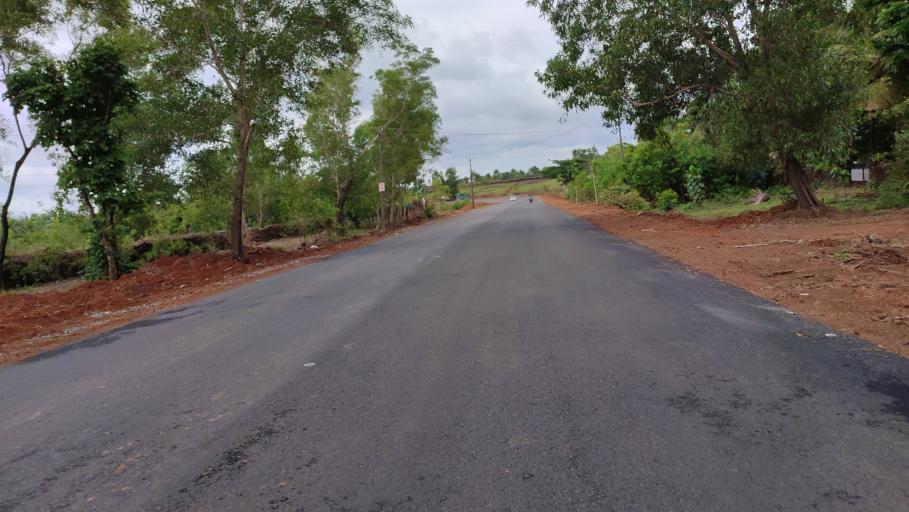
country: IN
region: Kerala
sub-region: Kasaragod District
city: Kasaragod
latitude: 12.5514
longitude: 75.0711
